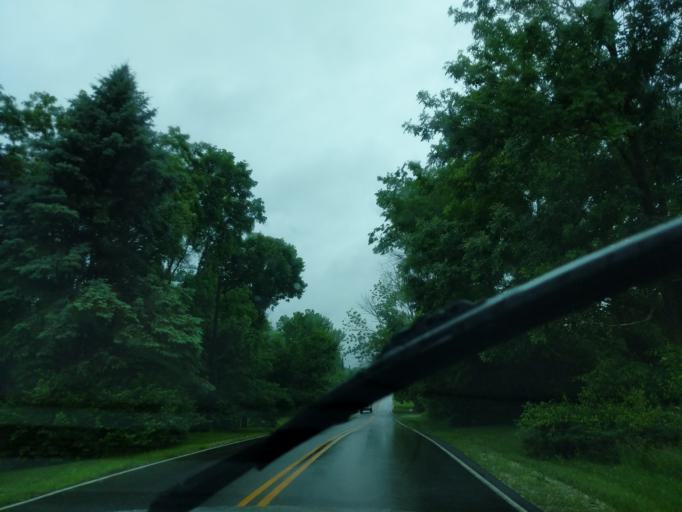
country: US
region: Indiana
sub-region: Madison County
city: Lapel
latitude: 40.0671
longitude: -85.8714
